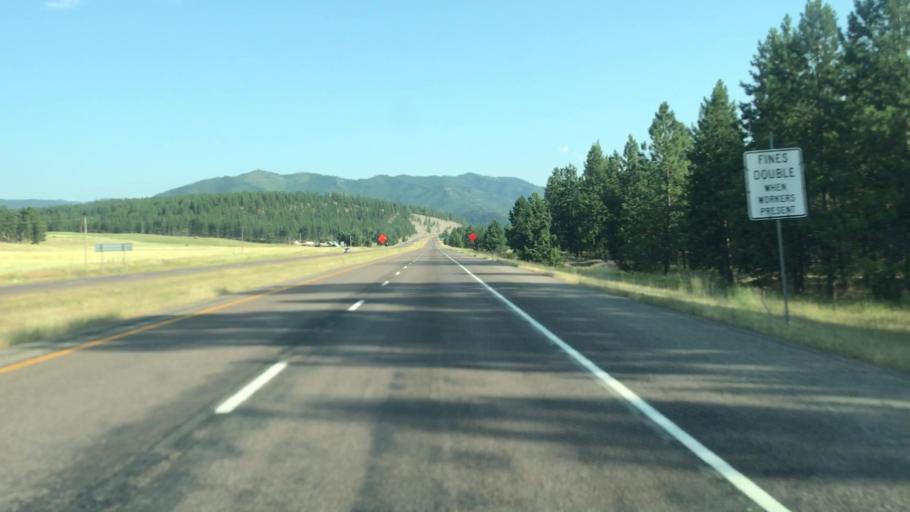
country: US
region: Montana
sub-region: Mineral County
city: Superior
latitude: 47.0357
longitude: -114.7461
